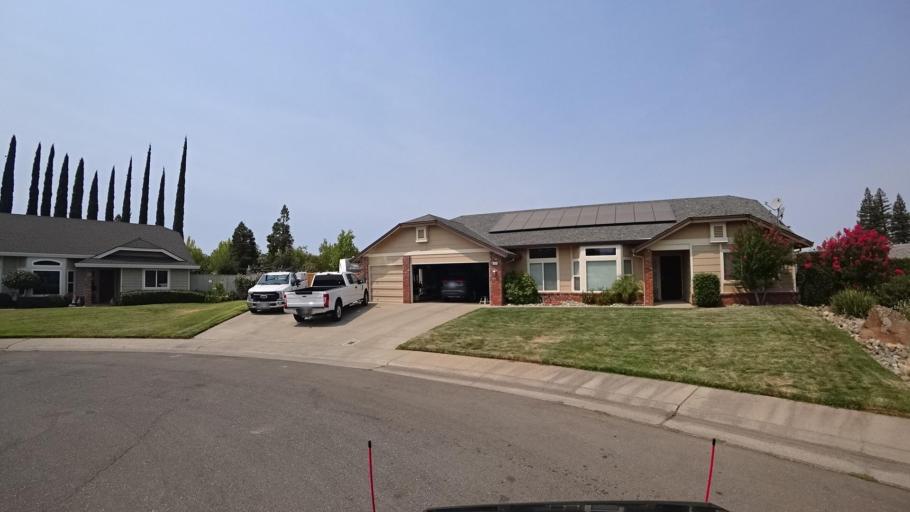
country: US
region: California
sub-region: Placer County
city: Rocklin
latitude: 38.7955
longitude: -121.2633
